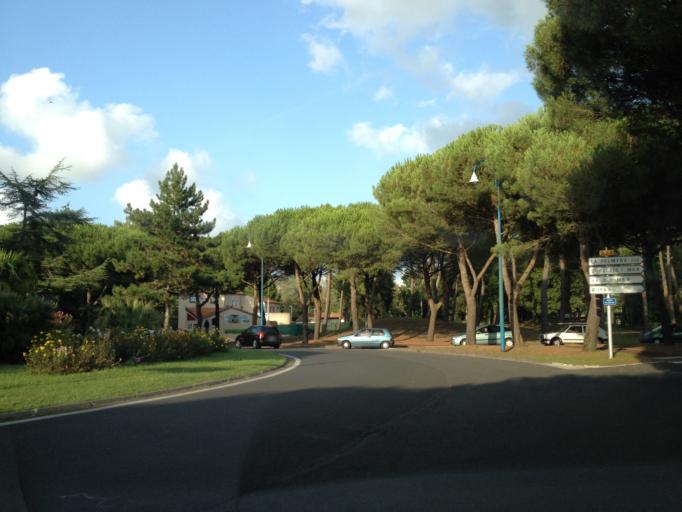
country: FR
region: Poitou-Charentes
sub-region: Departement de la Charente-Maritime
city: Les Mathes
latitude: 45.6907
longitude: -1.1793
